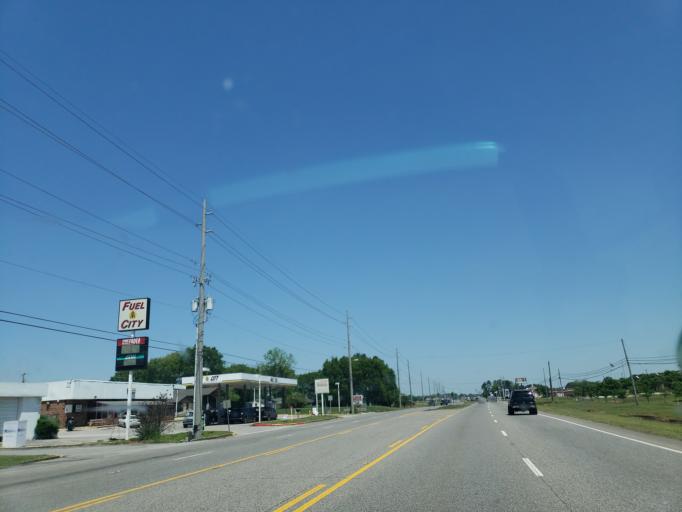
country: US
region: Alabama
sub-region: Madison County
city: Hazel Green
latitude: 34.9350
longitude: -86.5718
